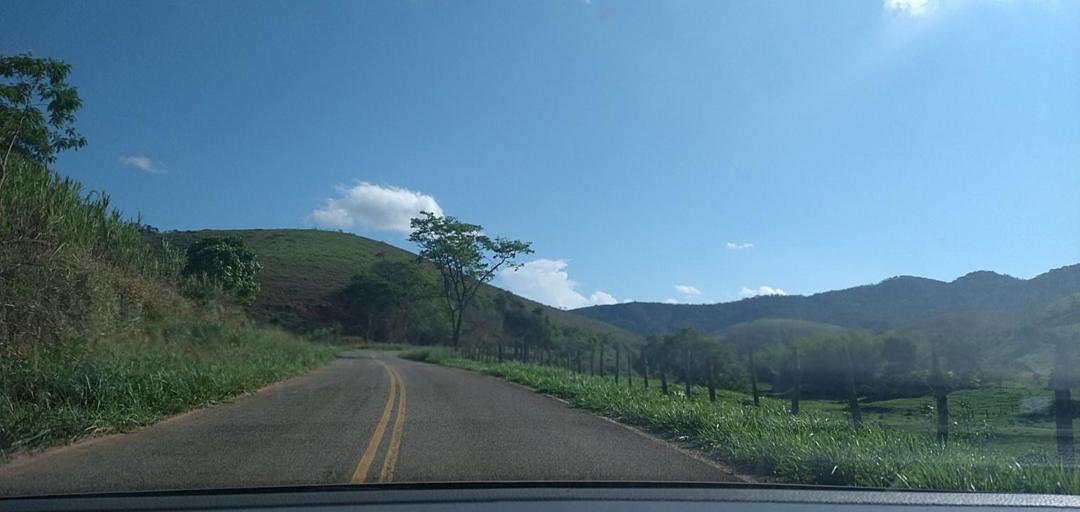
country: BR
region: Minas Gerais
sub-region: Alvinopolis
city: Alvinopolis
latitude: -20.1821
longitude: -42.9325
